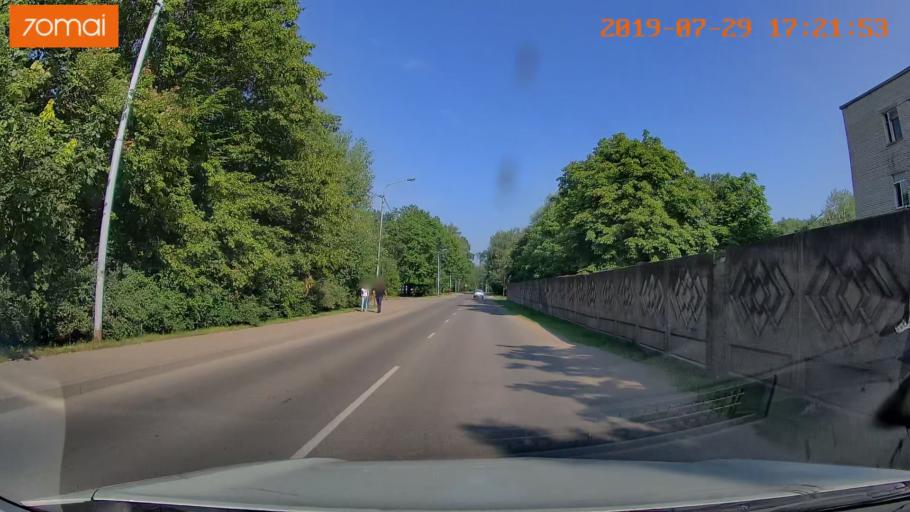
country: RU
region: Kaliningrad
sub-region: Gorod Kaliningrad
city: Kaliningrad
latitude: 54.7701
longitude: 20.4349
